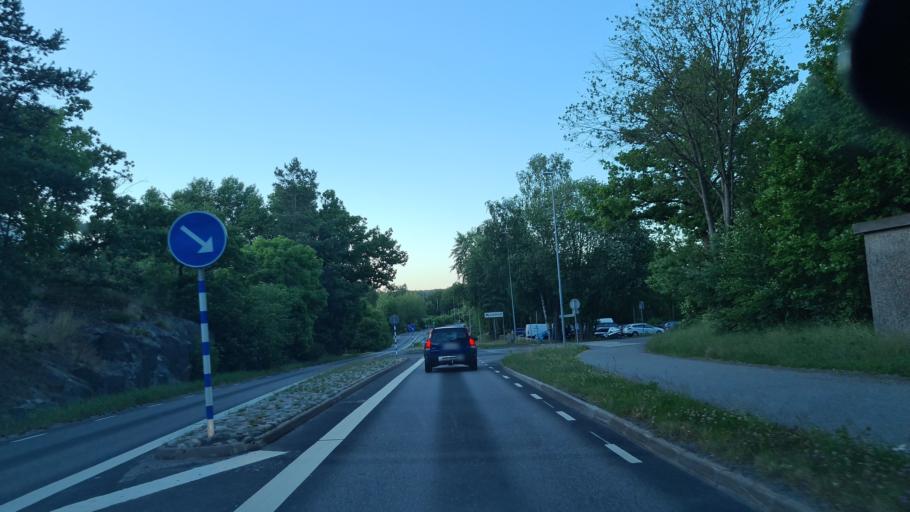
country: SE
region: Stockholm
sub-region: Nacka Kommun
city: Alta
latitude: 59.2539
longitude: 18.1779
